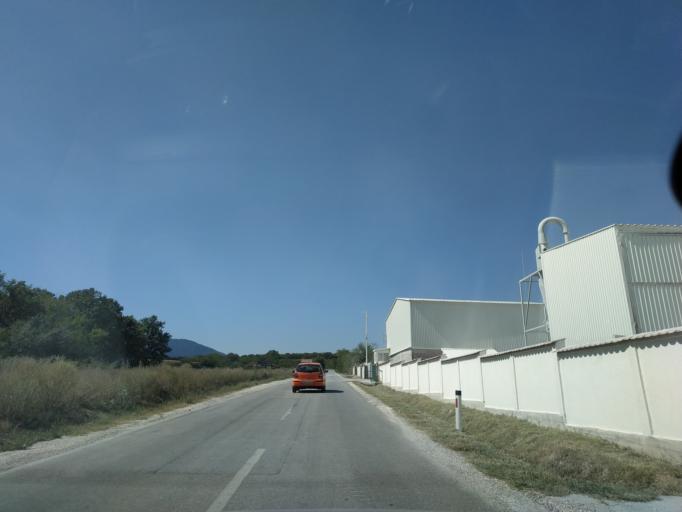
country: RS
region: Central Serbia
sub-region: Sumadijski Okrug
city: Arangelovac
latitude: 44.2966
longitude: 20.5912
